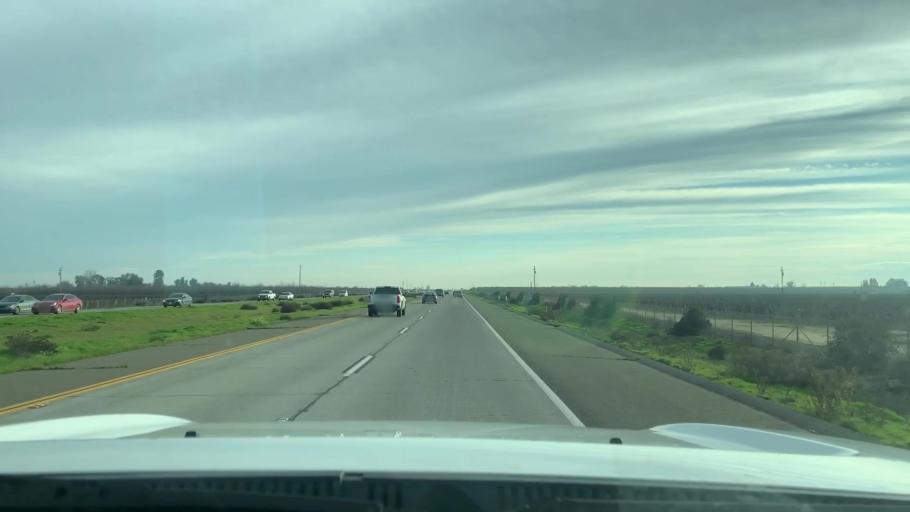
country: US
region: California
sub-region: Fresno County
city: Caruthers
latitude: 36.5392
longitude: -119.7864
